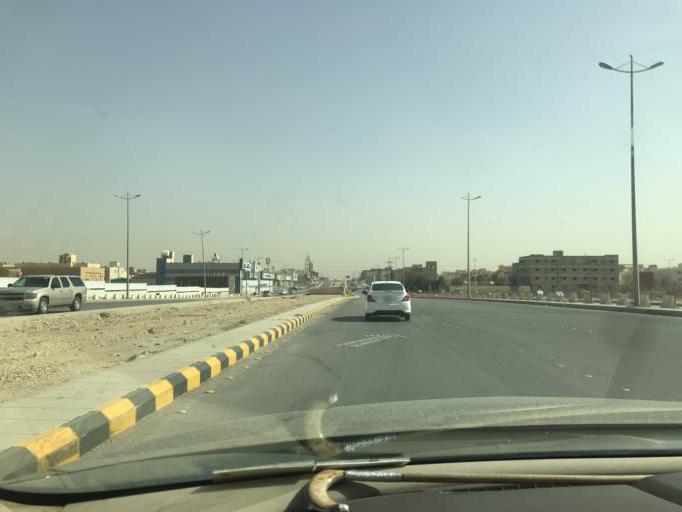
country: SA
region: Ar Riyad
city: Riyadh
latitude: 24.8259
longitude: 46.7273
